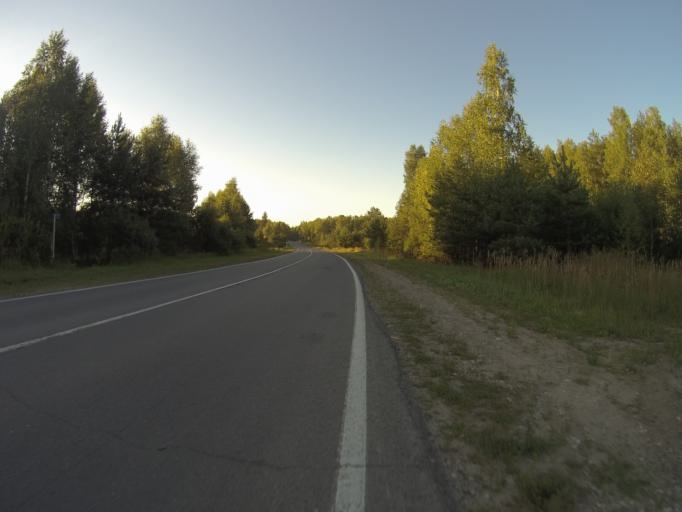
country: RU
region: Vladimir
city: Anopino
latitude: 55.7244
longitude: 40.7267
